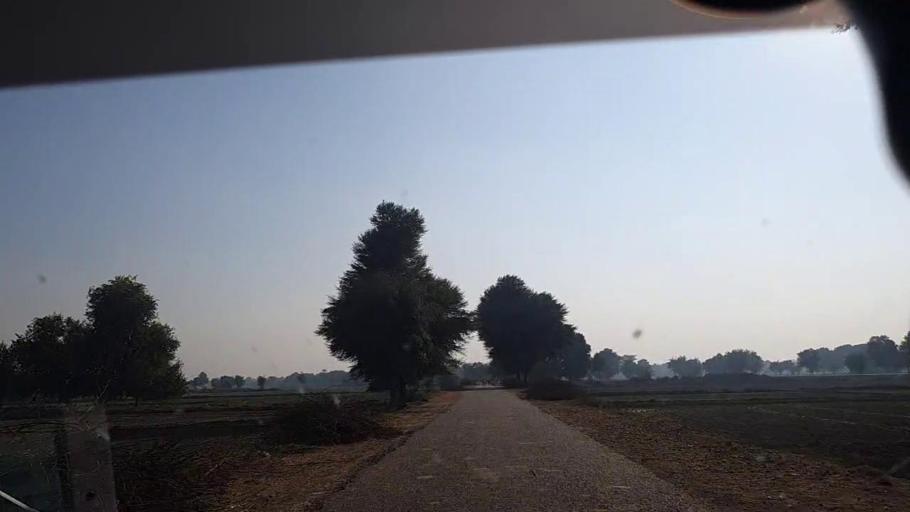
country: PK
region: Sindh
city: Hingorja
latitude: 27.2303
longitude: 68.2692
